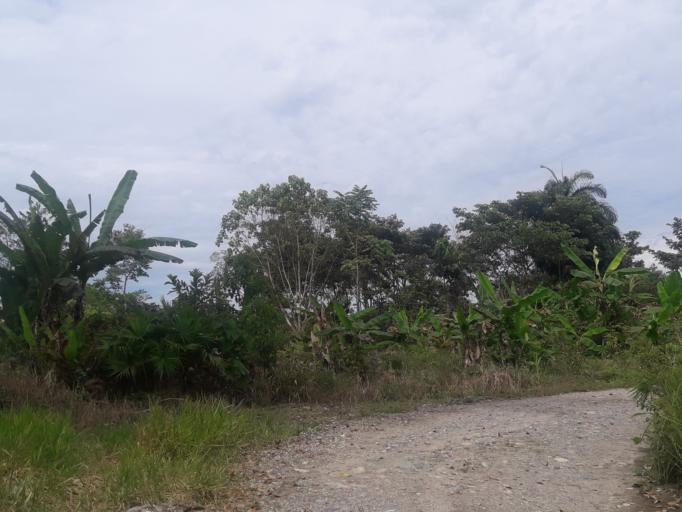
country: EC
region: Napo
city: Tena
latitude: -1.0576
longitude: -77.7929
